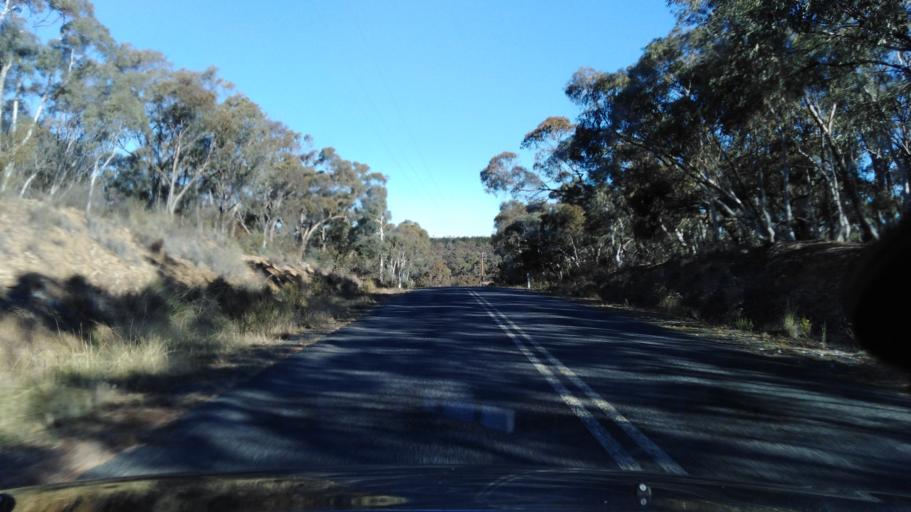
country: AU
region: New South Wales
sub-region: Palerang
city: Bungendore
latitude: -35.2063
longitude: 149.3453
